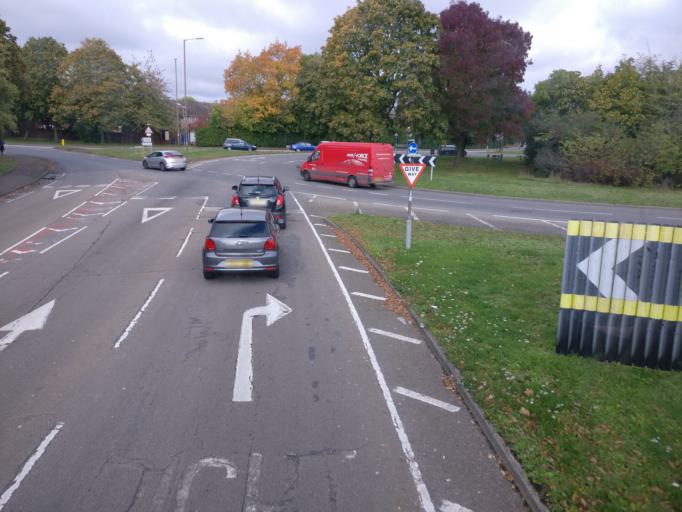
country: GB
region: England
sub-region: Surrey
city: Frimley
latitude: 51.3079
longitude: -0.7506
